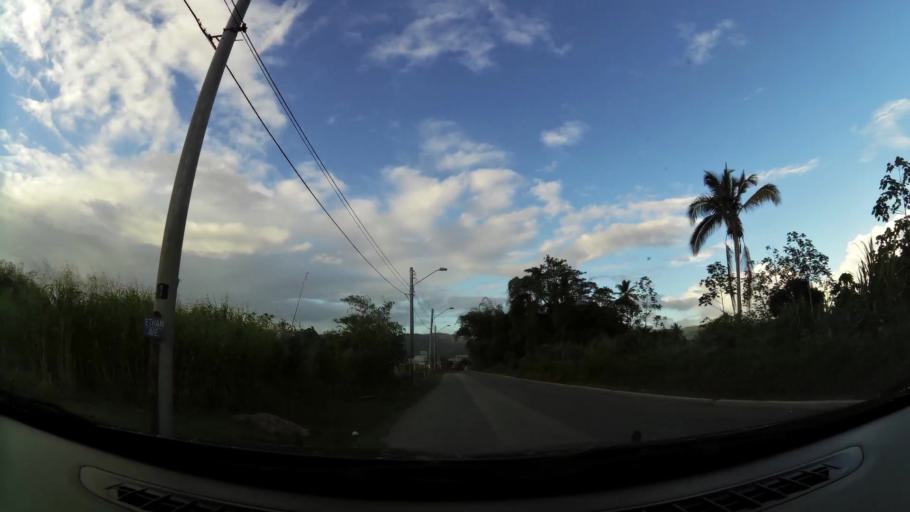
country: TT
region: Tunapuna/Piarco
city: Arouca
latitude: 10.6127
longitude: -61.3457
